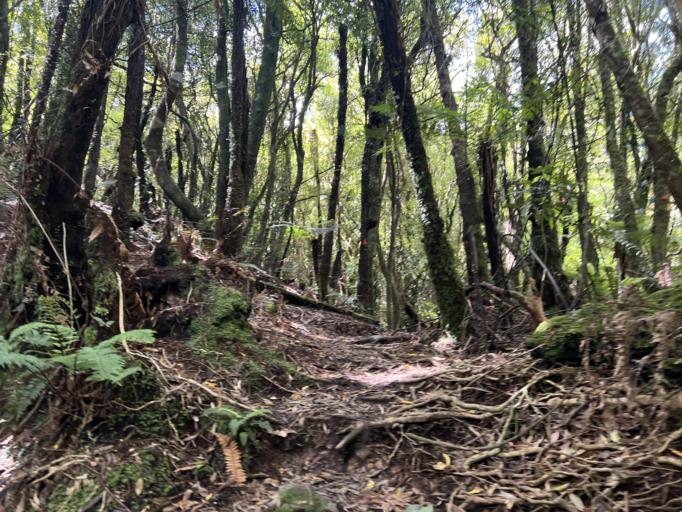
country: NZ
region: Wellington
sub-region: Kapiti Coast District
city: Paraparaumu
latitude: -40.8803
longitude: 175.0903
